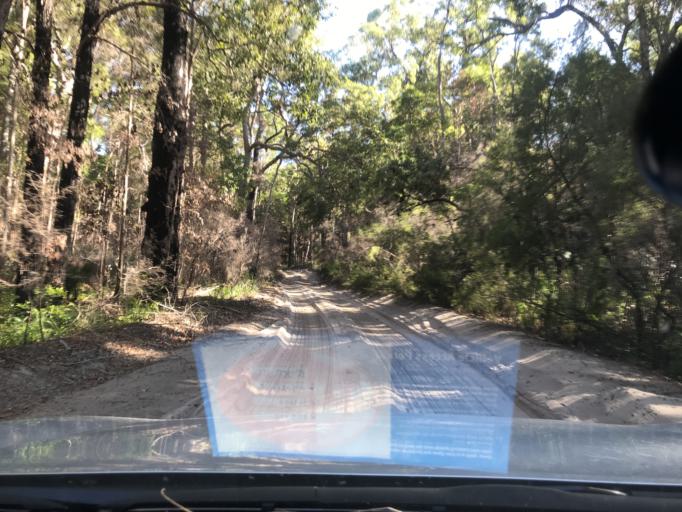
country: AU
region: Queensland
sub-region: Fraser Coast
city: Urangan
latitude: -25.4987
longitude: 153.0992
